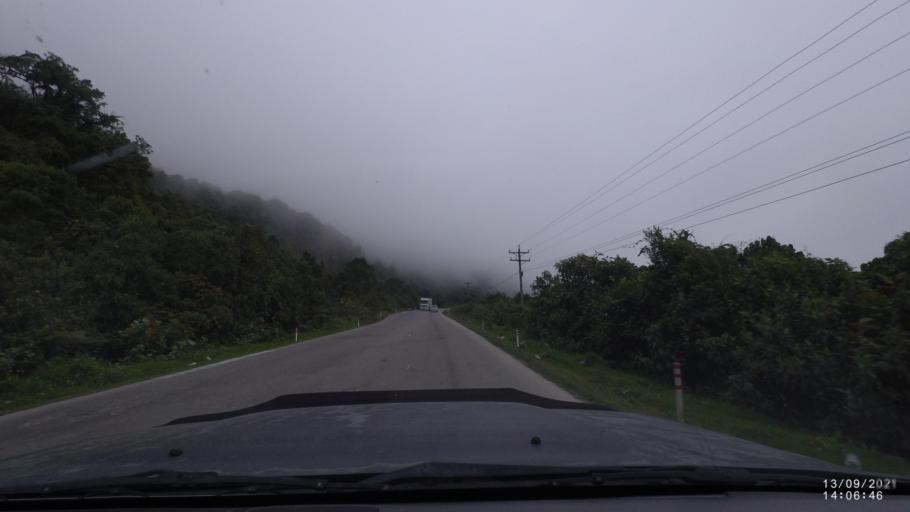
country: BO
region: Cochabamba
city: Colomi
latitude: -17.1853
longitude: -65.8851
